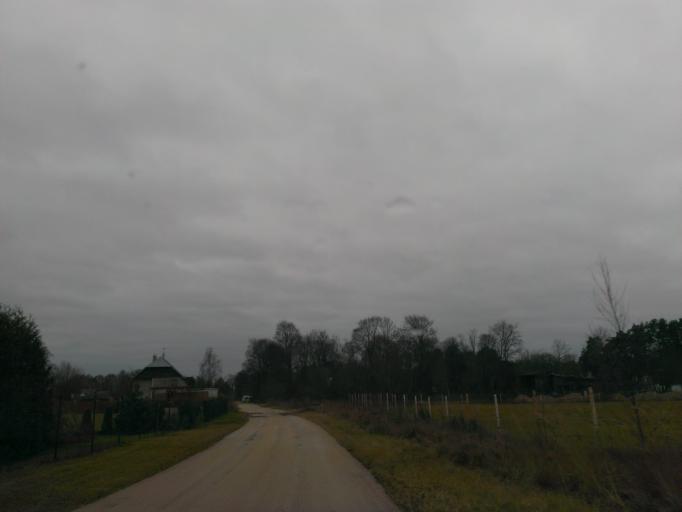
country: LV
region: Adazi
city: Adazi
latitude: 57.0778
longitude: 24.3451
